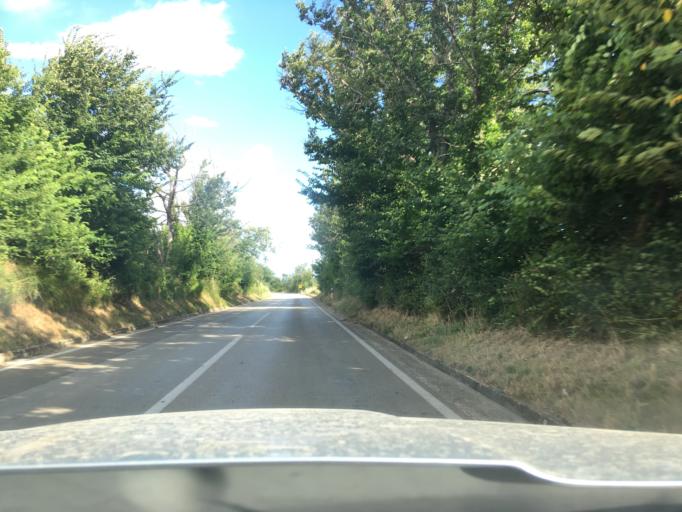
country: HR
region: Zadarska
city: Nin
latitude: 44.2350
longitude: 15.1874
